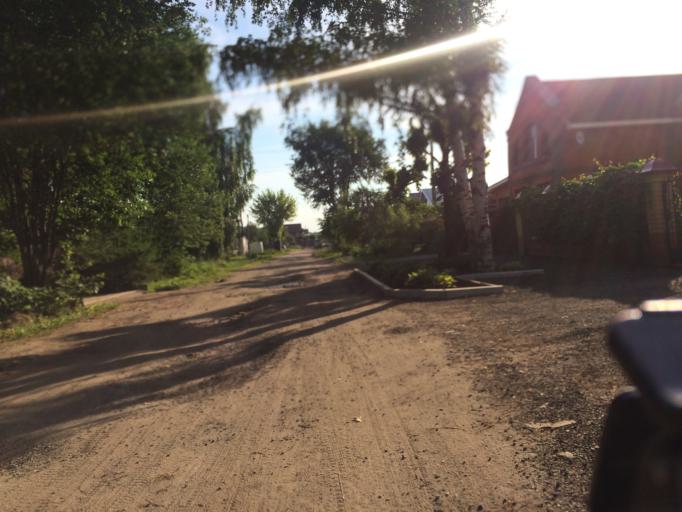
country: RU
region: Mariy-El
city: Yoshkar-Ola
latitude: 56.6493
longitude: 47.9162
